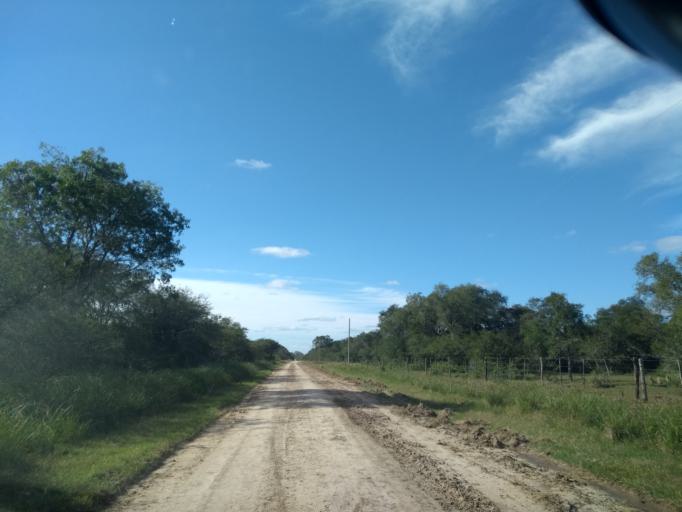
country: AR
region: Chaco
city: Colonia Benitez
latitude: -27.2859
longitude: -58.9301
